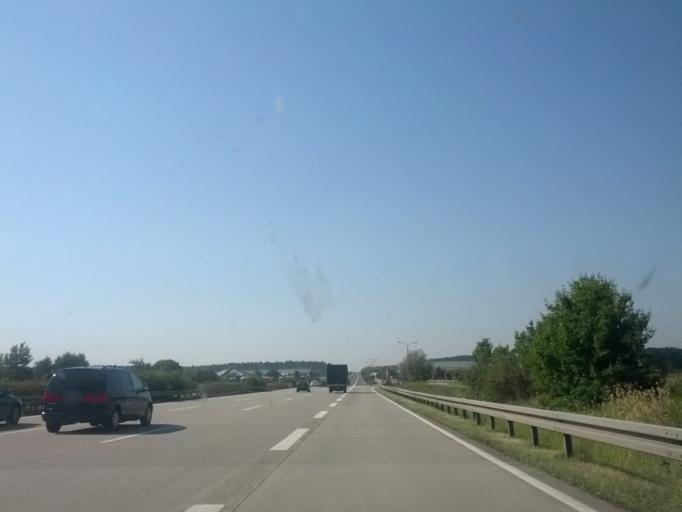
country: DE
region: Brandenburg
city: Linthe
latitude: 52.1367
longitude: 12.7567
